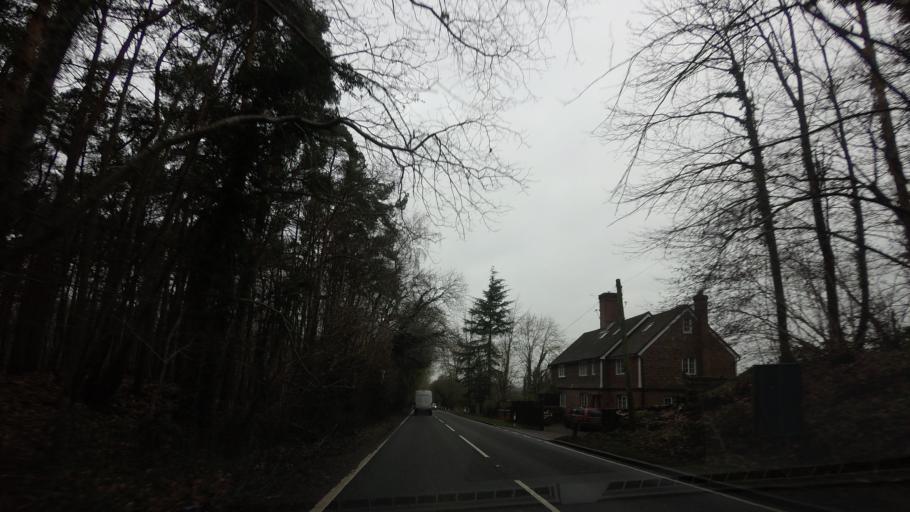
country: GB
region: England
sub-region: Kent
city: Staplehurst
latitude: 51.1297
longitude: 0.5605
